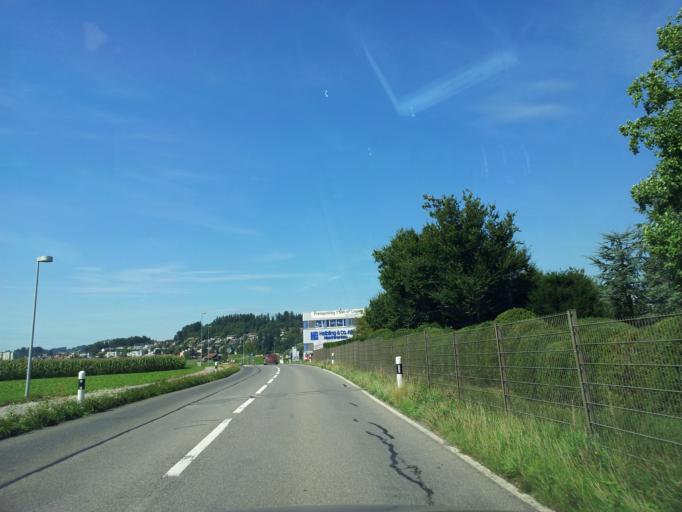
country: CH
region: Saint Gallen
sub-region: Wahlkreis See-Gaster
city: Jona
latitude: 47.2229
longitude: 8.8645
